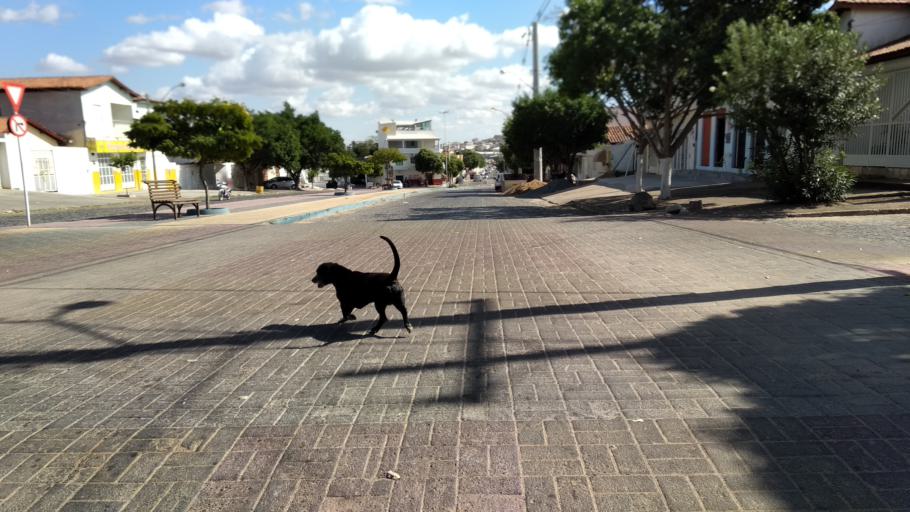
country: BR
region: Bahia
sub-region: Guanambi
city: Guanambi
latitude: -14.2361
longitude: -42.7772
